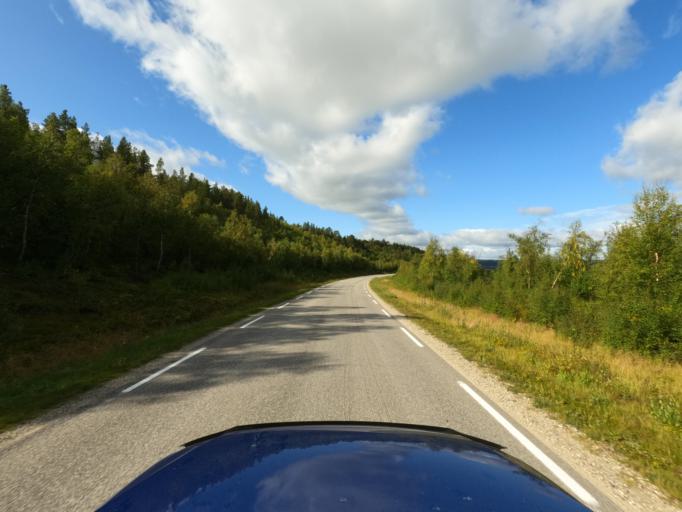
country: NO
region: Finnmark Fylke
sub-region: Karasjok
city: Karasjohka
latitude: 69.4490
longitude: 25.5908
